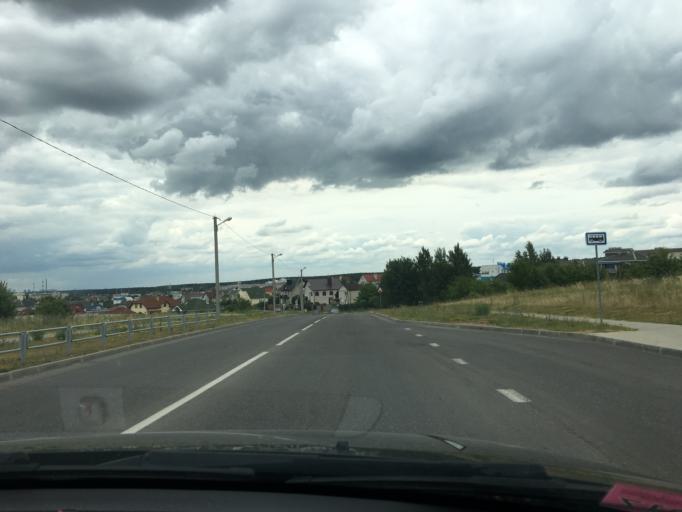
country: BY
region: Grodnenskaya
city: Hrodna
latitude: 53.6197
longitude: 23.8336
